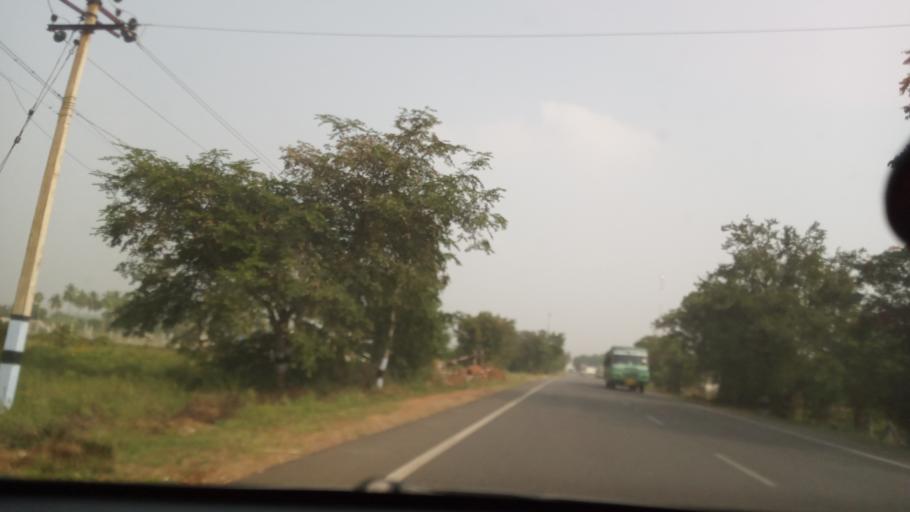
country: IN
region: Tamil Nadu
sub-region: Erode
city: Punjai Puliyampatti
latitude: 11.3746
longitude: 77.1716
